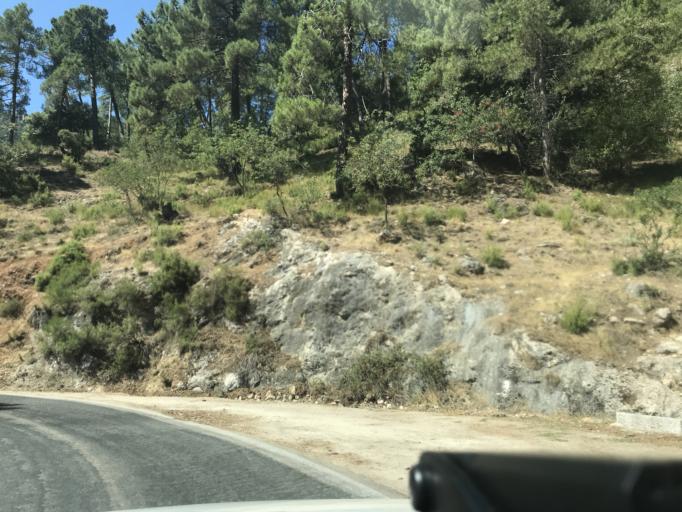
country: ES
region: Andalusia
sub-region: Provincia de Jaen
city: La Iruela
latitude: 37.9191
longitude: -2.9536
